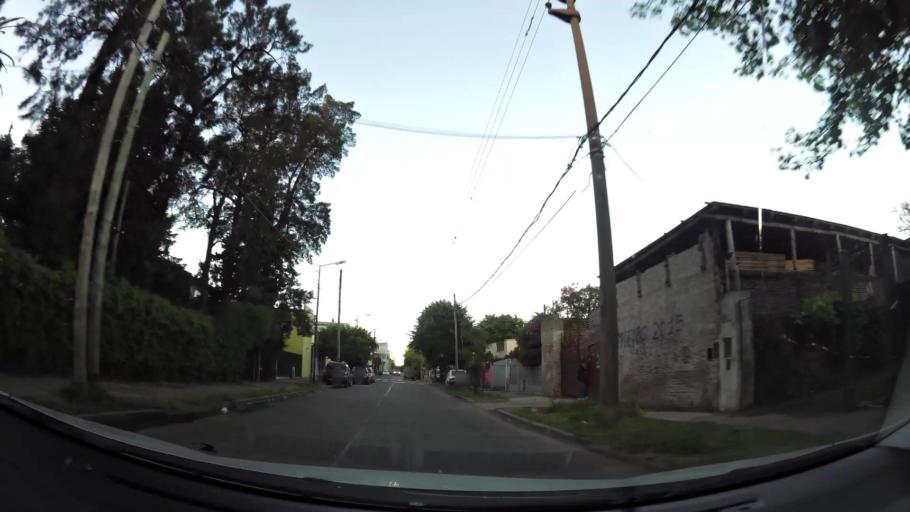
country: AR
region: Buenos Aires
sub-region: Partido de Tigre
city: Tigre
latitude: -34.4432
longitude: -58.5721
